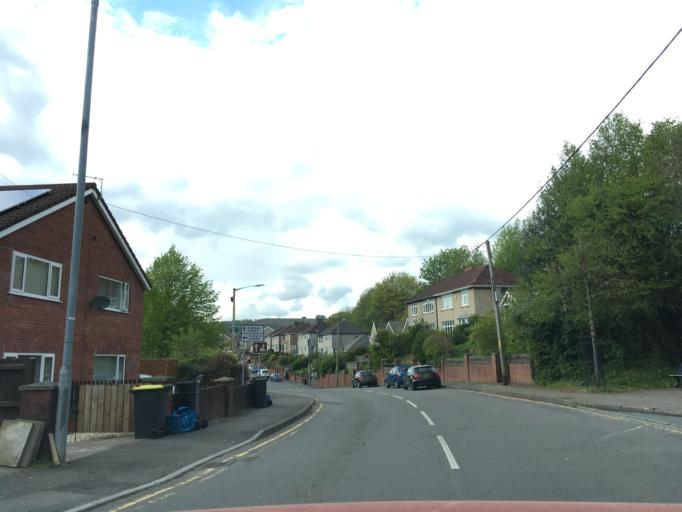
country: GB
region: Wales
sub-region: Merthyr Tydfil County Borough
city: Treharris
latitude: 51.6641
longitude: -3.2935
